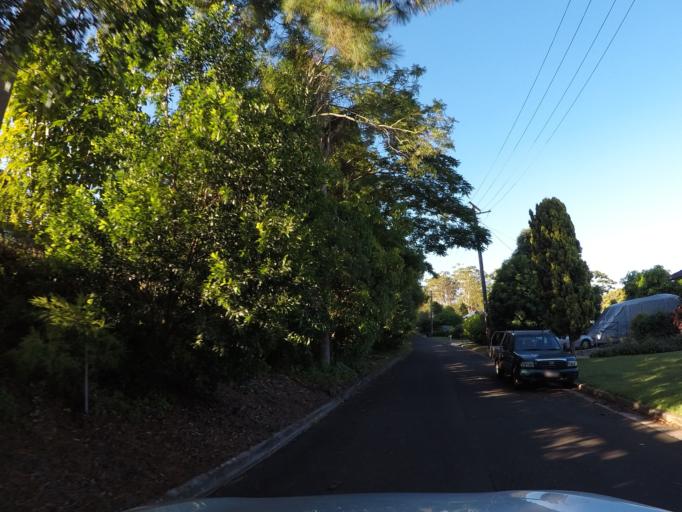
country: AU
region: Queensland
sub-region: Sunshine Coast
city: Nambour
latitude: -26.6354
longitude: 152.8702
